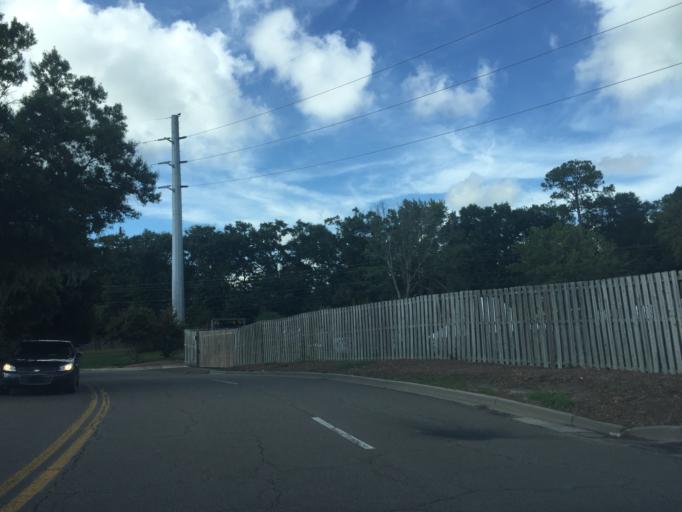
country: US
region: Georgia
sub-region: Chatham County
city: Georgetown
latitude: 31.9840
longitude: -81.1688
